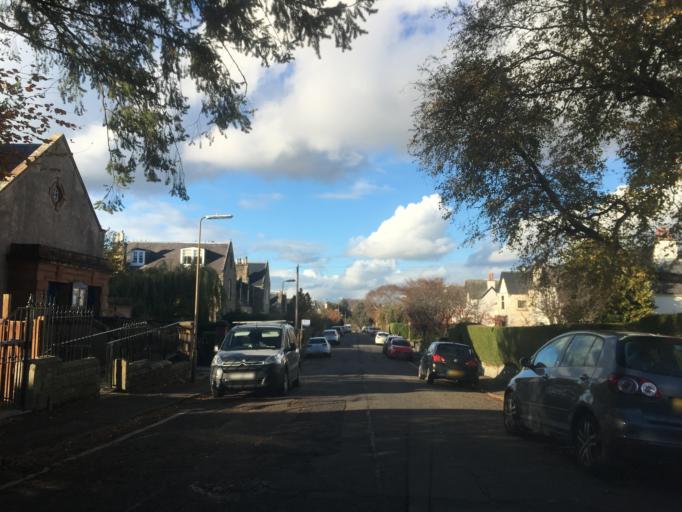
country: GB
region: Scotland
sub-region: Edinburgh
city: Colinton
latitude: 55.9056
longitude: -3.2539
